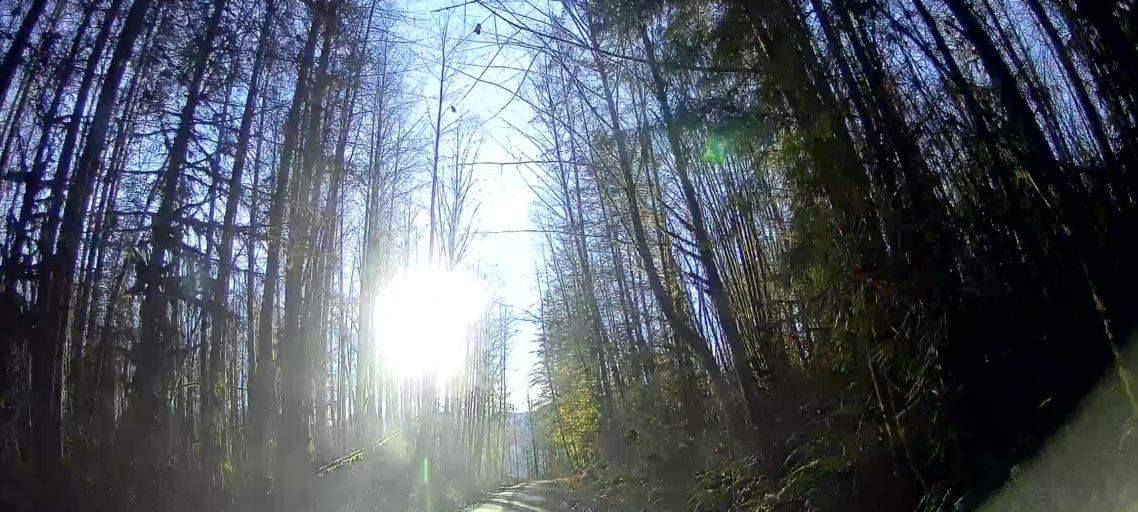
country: US
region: Washington
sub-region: Snohomish County
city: Darrington
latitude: 48.5418
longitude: -121.7273
